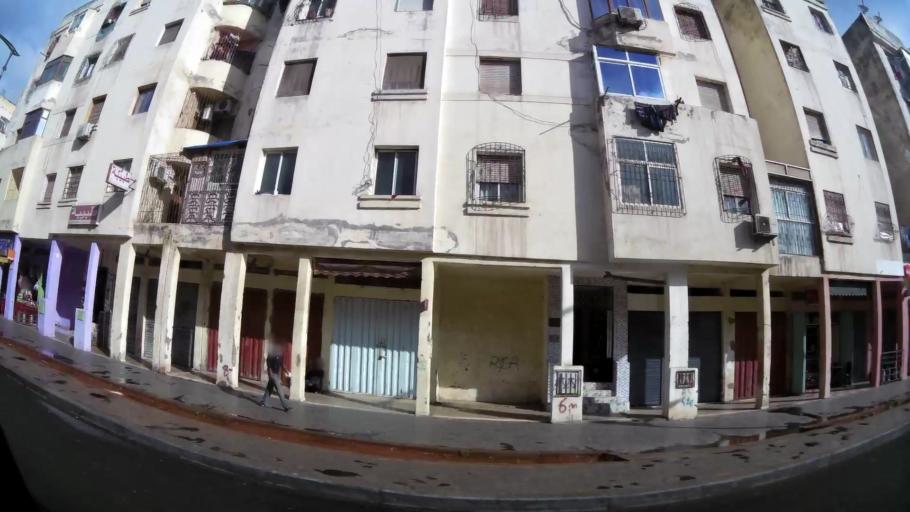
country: MA
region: Grand Casablanca
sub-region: Mediouna
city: Tit Mellil
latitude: 33.5958
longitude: -7.5380
